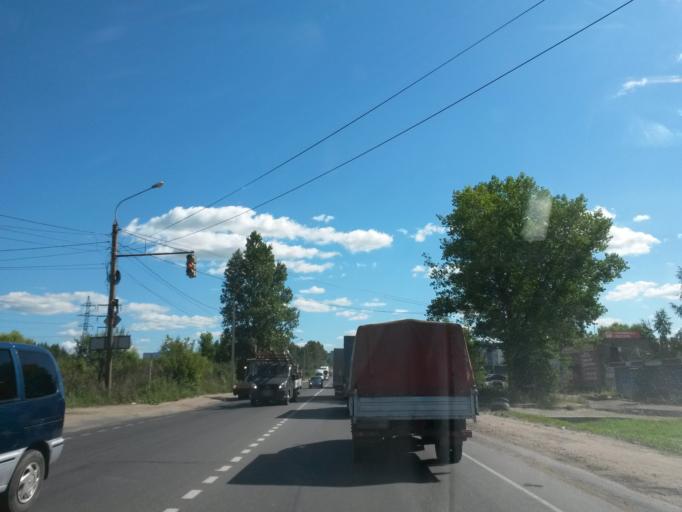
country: RU
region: Jaroslavl
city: Yaroslavl
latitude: 57.5944
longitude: 39.8126
